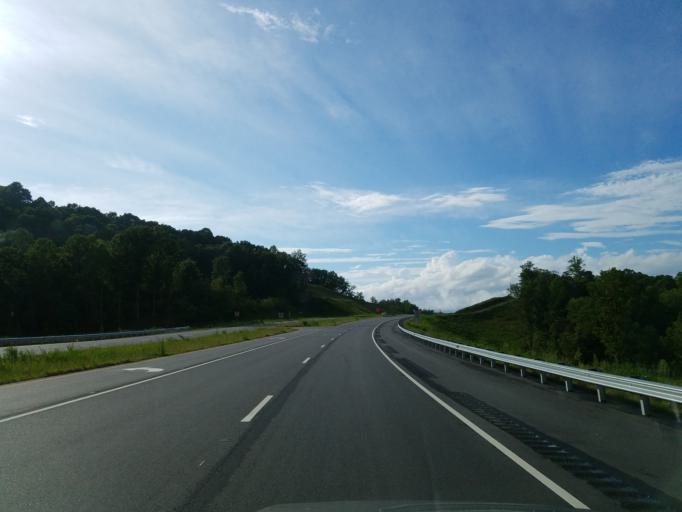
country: US
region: Georgia
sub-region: White County
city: Cleveland
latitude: 34.5839
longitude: -83.7742
